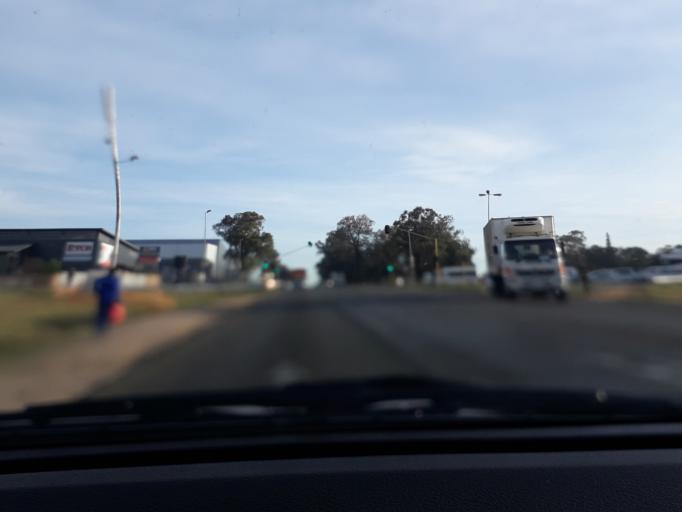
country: ZA
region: Gauteng
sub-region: City of Johannesburg Metropolitan Municipality
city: Midrand
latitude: -25.9440
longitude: 28.1438
